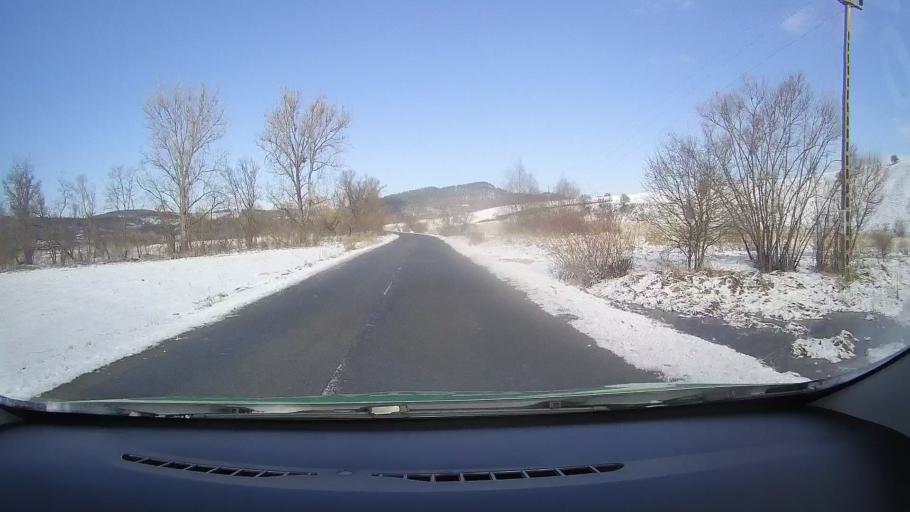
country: RO
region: Sibiu
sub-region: Comuna Mihaileni
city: Mihaileni
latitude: 45.9988
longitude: 24.3611
